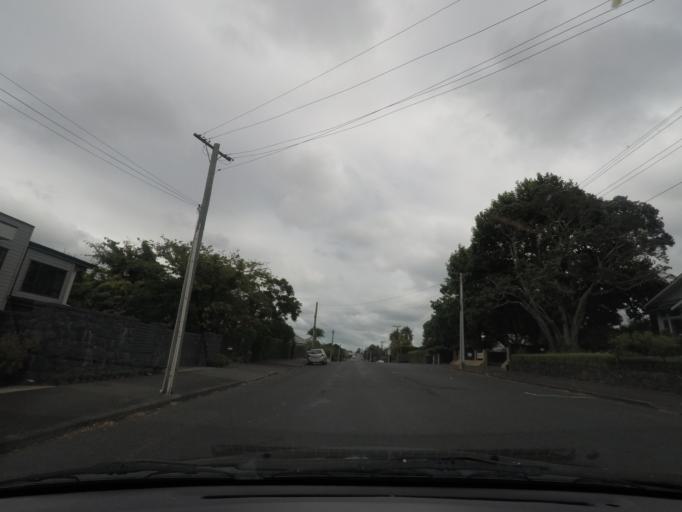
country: NZ
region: Auckland
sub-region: Auckland
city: Auckland
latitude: -36.8825
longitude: 174.7906
